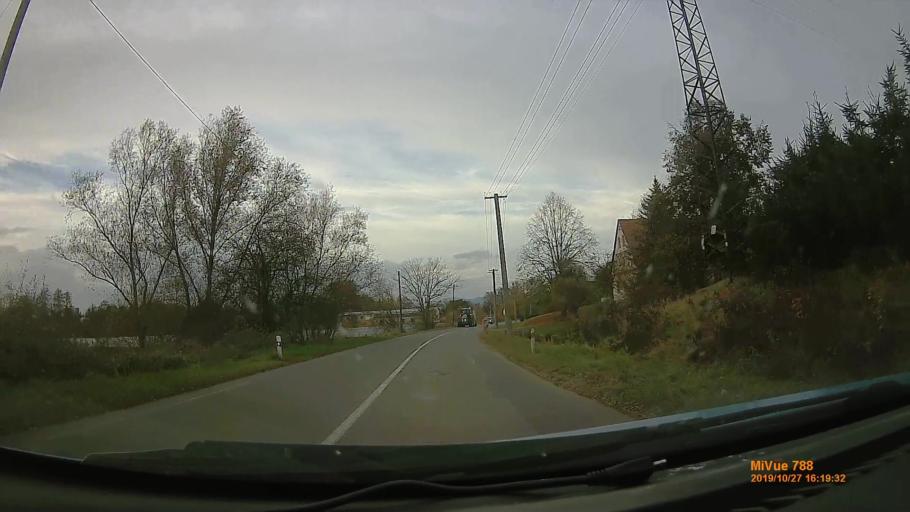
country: CZ
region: Kralovehradecky
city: Broumov
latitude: 50.5734
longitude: 16.3439
